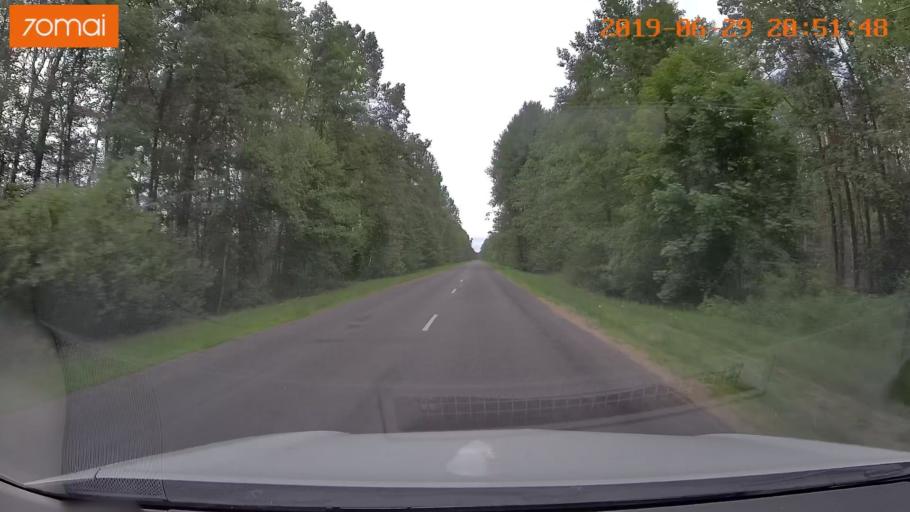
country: BY
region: Brest
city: Hantsavichy
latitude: 52.6923
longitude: 26.3544
